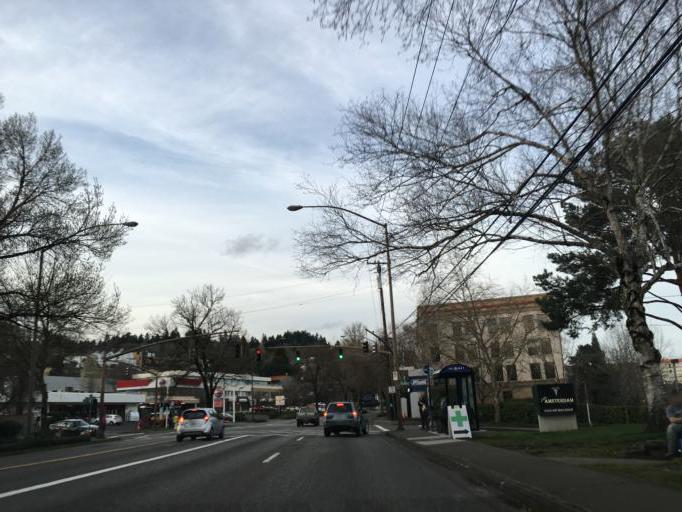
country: US
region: Oregon
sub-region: Multnomah County
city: Portland
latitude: 45.4846
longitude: -122.6748
